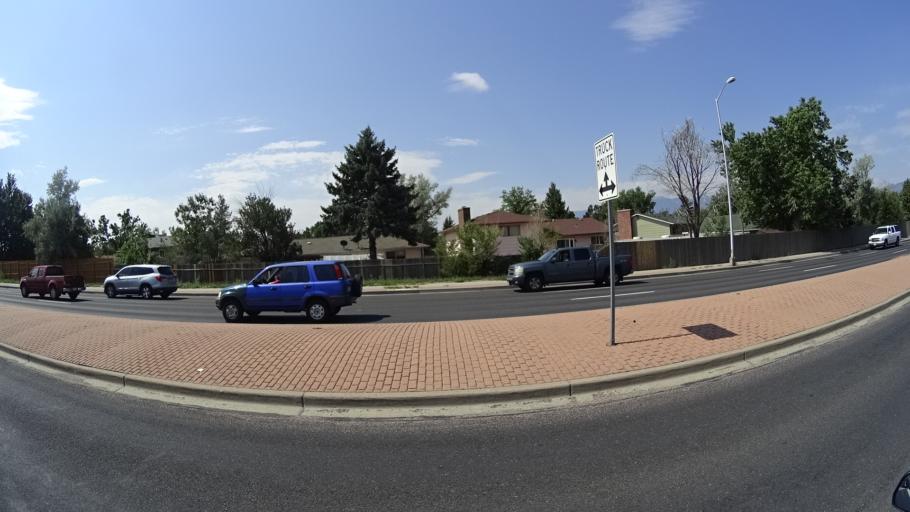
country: US
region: Colorado
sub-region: El Paso County
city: Colorado Springs
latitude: 38.9034
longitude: -104.7727
